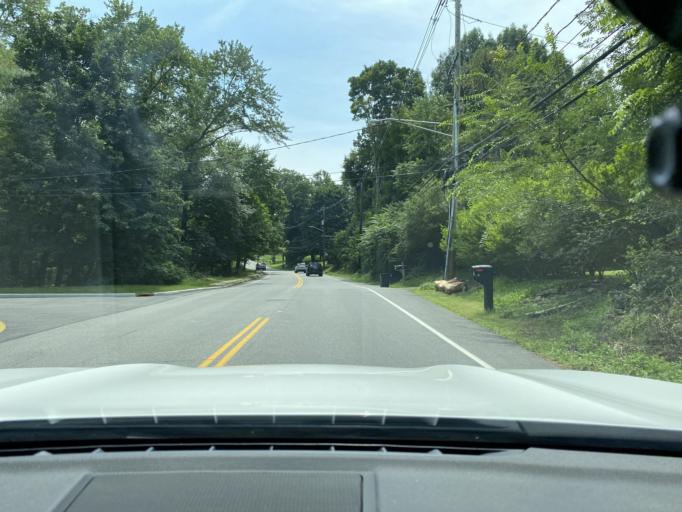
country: US
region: New York
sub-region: Rockland County
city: Airmont
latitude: 41.1097
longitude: -74.1147
